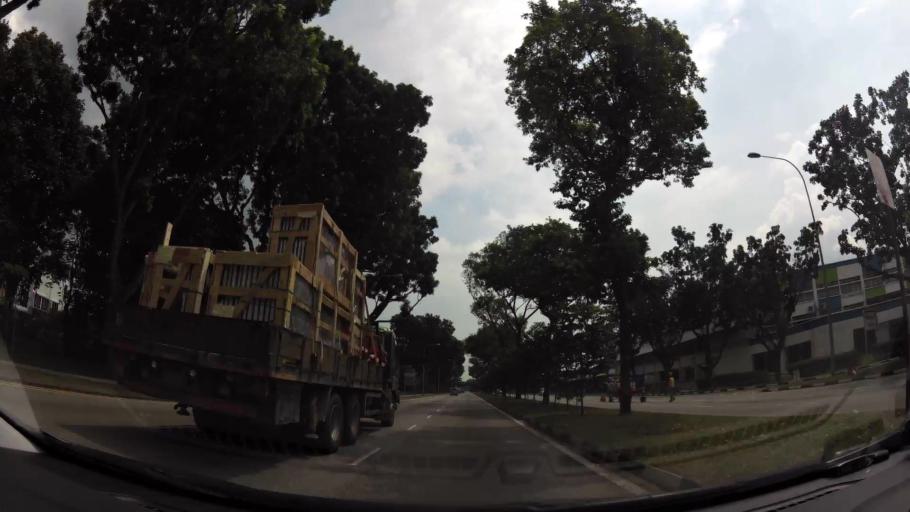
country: SG
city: Singapore
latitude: 1.2861
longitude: 103.7792
